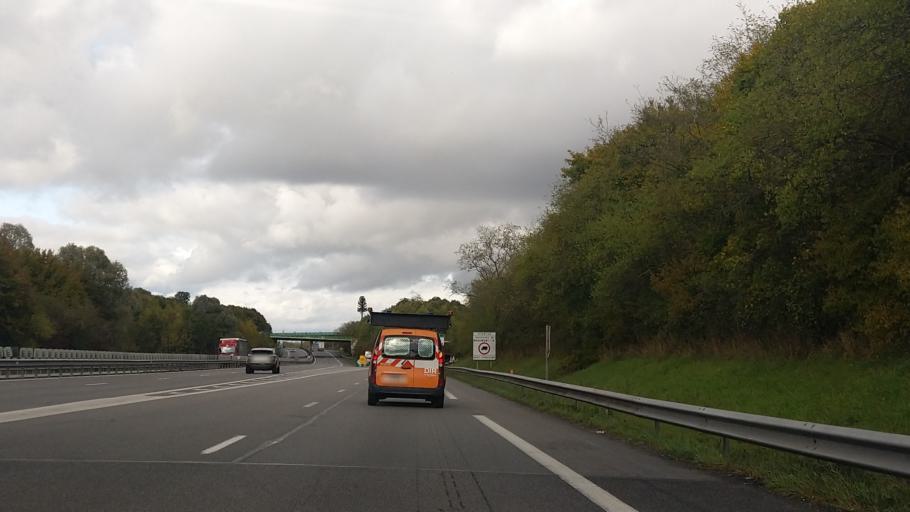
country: FR
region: Ile-de-France
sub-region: Departement du Val-d'Oise
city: Mours
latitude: 49.1224
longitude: 2.2531
